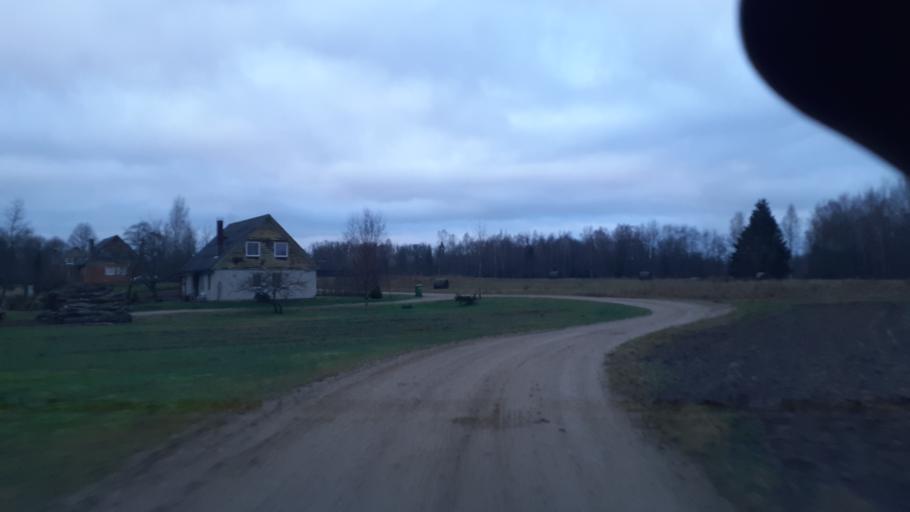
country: LV
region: Alsunga
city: Alsunga
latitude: 56.9049
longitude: 21.6992
